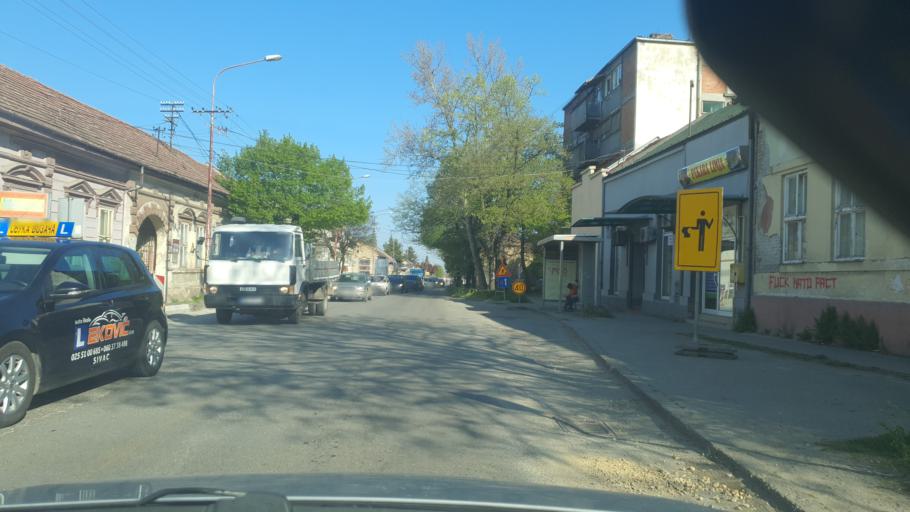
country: RS
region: Autonomna Pokrajina Vojvodina
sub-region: Zapadnobacki Okrug
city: Kula
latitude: 45.6131
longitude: 19.5270
